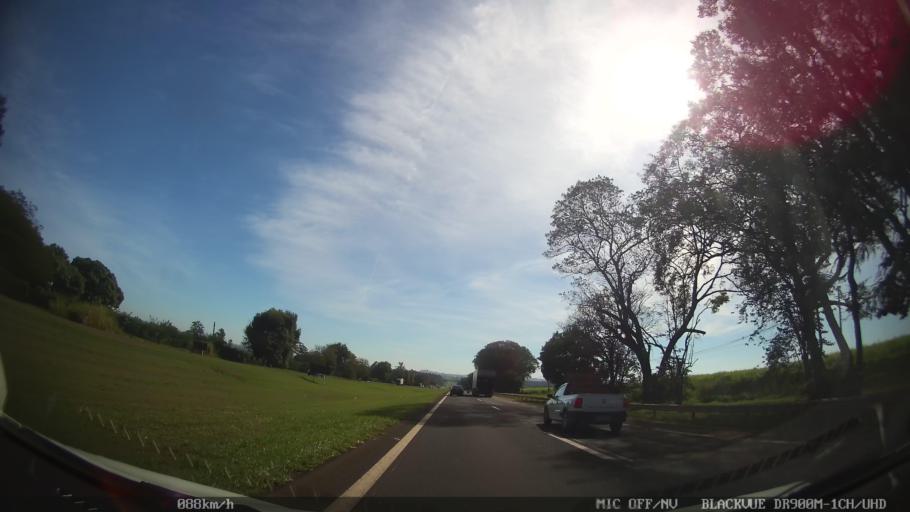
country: BR
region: Sao Paulo
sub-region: Leme
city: Leme
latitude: -22.2433
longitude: -47.3904
